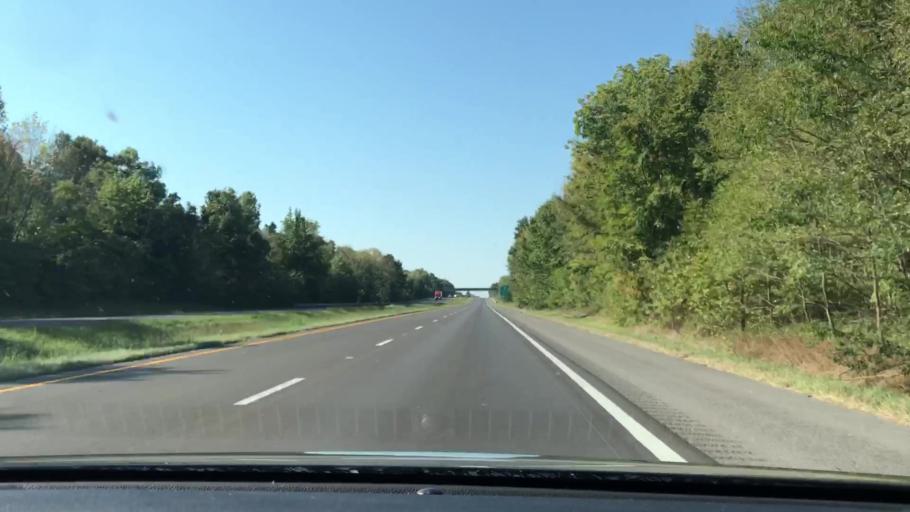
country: US
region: Kentucky
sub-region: Graves County
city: Mayfield
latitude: 36.6722
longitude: -88.7371
